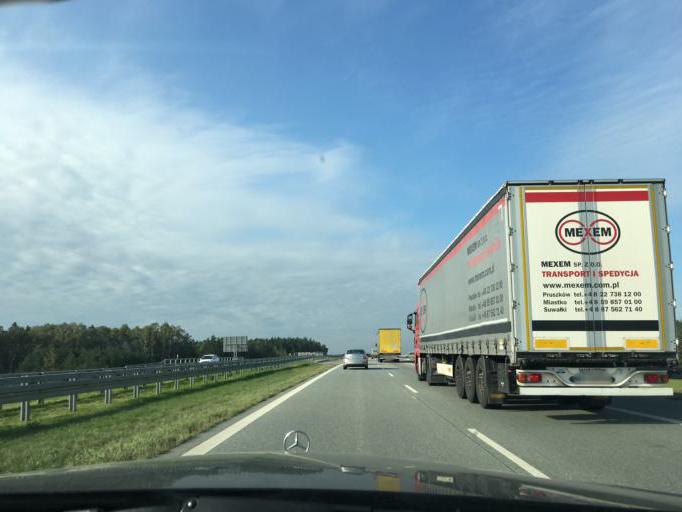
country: PL
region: Lodz Voivodeship
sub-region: Powiat laski
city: Lask
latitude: 51.5694
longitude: 19.1679
